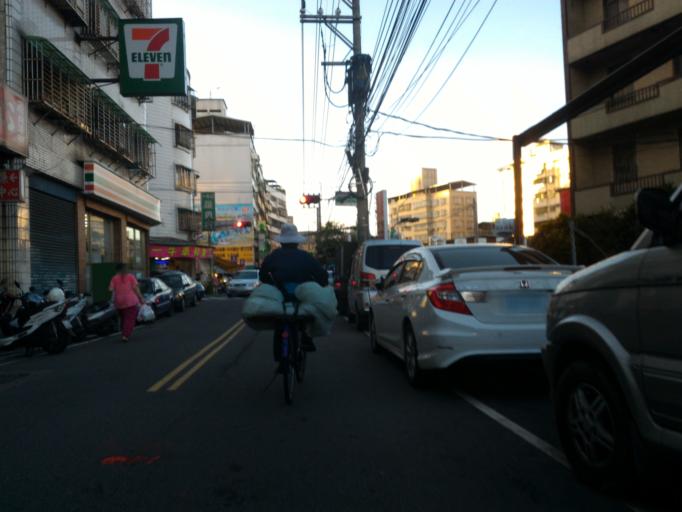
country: TW
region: Taipei
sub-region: Taipei
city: Banqiao
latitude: 24.9777
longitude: 121.4186
